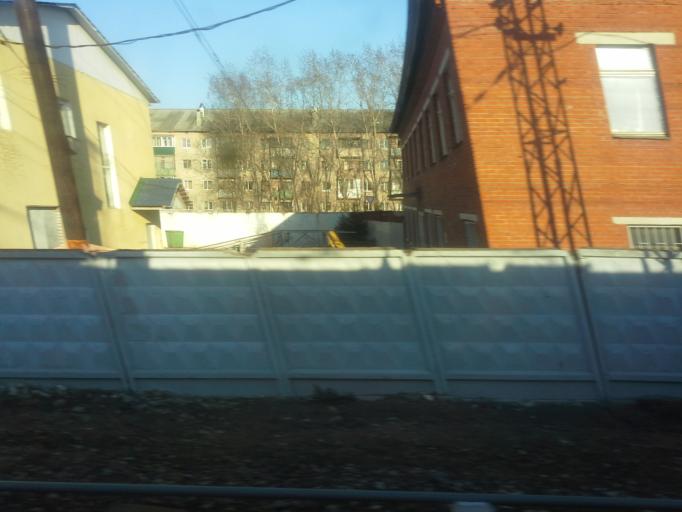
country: RU
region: Moskovskaya
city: Nekrasovskiy
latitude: 56.0875
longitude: 37.5027
